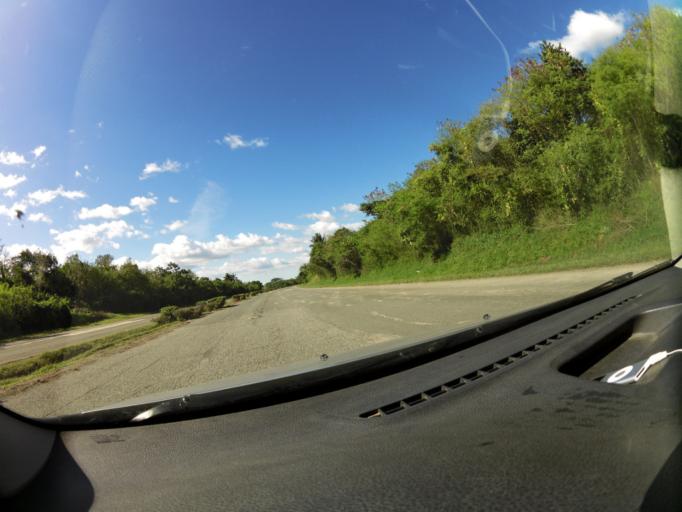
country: CU
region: Santiago de Cuba
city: San Luis
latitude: 20.1407
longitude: -75.7699
